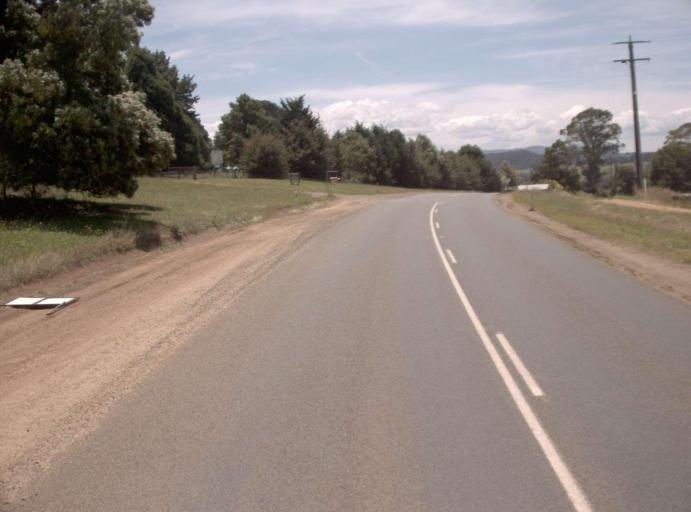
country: AU
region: Victoria
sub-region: Baw Baw
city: Warragul
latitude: -37.9841
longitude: 145.9446
